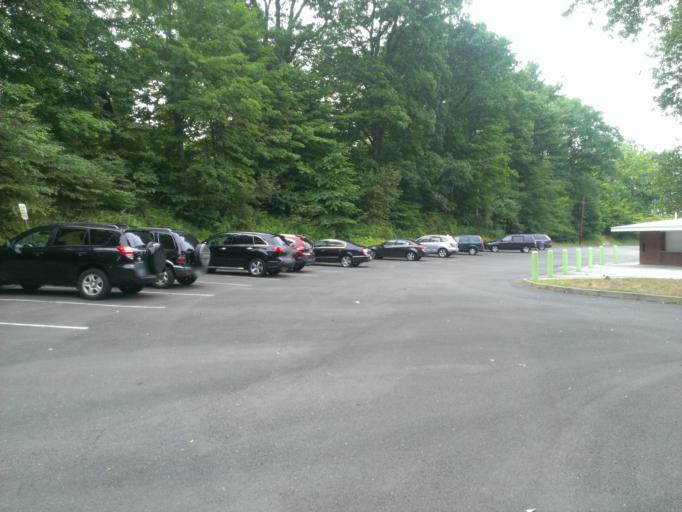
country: US
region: Connecticut
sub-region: New Haven County
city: Wallingford
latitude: 41.4720
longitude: -72.8077
